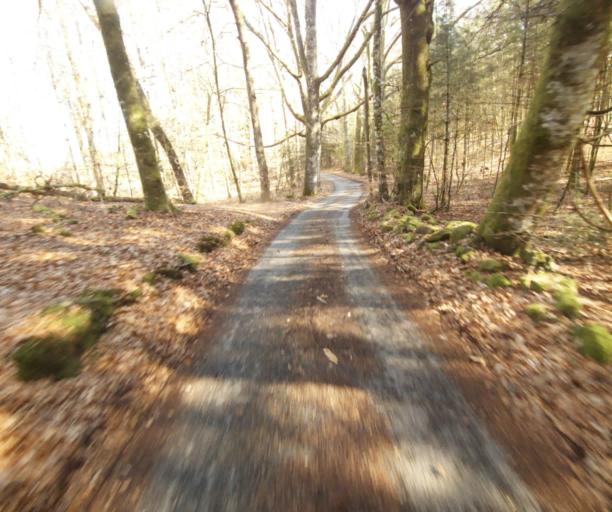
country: FR
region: Limousin
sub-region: Departement de la Correze
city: Correze
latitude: 45.2683
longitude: 1.9206
